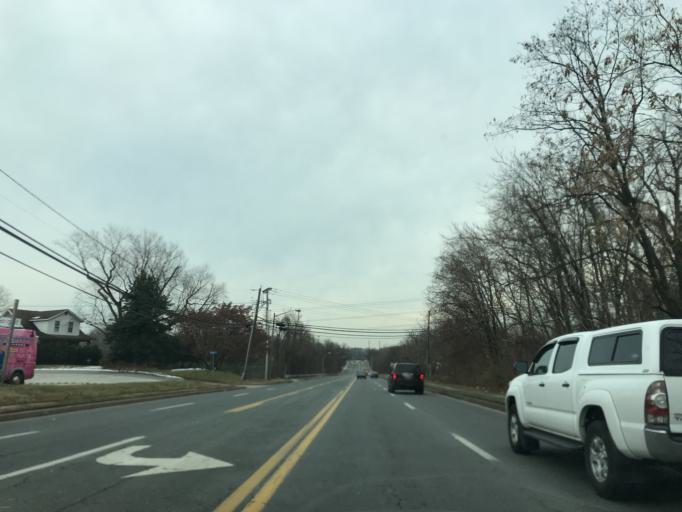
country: US
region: Maryland
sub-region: Baltimore County
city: Rossville
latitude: 39.3336
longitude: -76.4764
